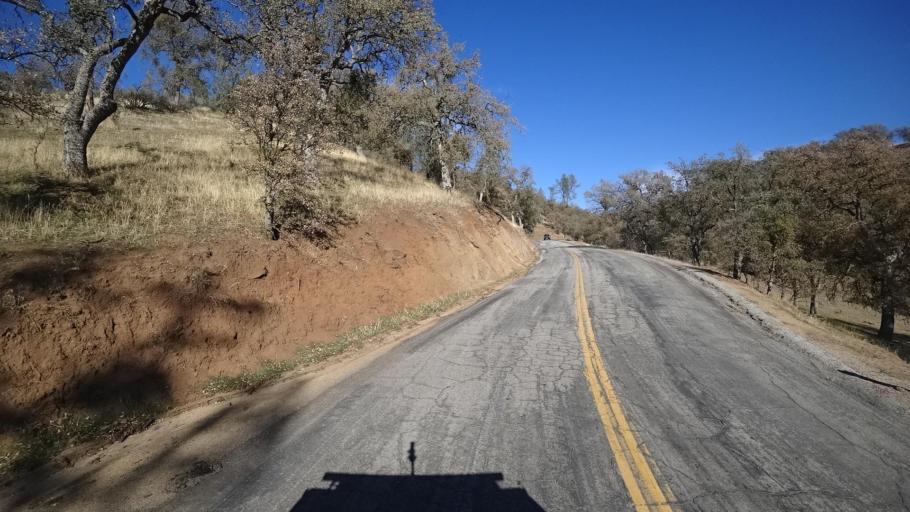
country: US
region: California
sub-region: Kern County
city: Bear Valley Springs
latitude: 35.3529
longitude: -118.5689
